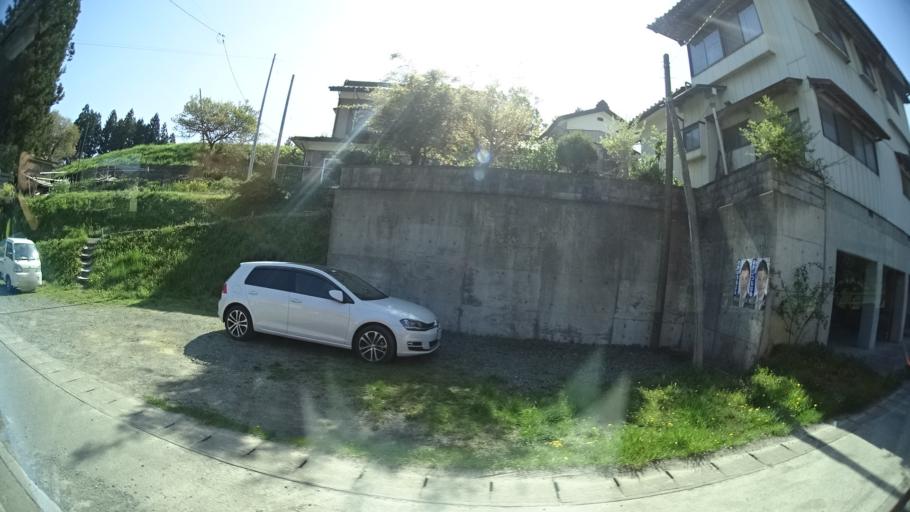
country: JP
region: Iwate
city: Ofunato
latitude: 38.9586
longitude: 141.6310
